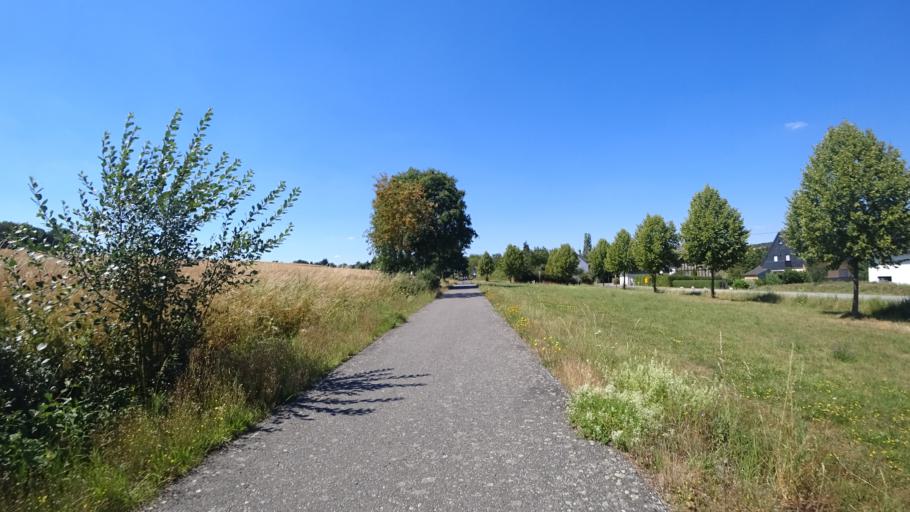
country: DE
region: Rheinland-Pfalz
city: Alterkulz
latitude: 50.0265
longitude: 7.4725
